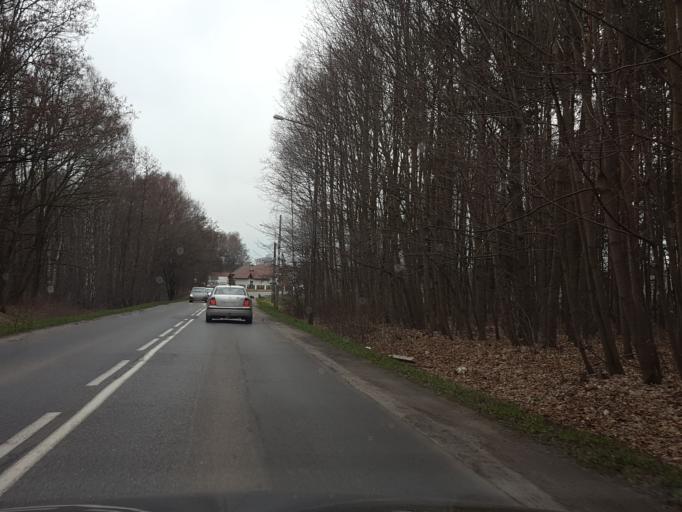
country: PL
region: Silesian Voivodeship
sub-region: Ruda Slaska
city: Ruda Slaska
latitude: 50.2300
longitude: 18.8333
